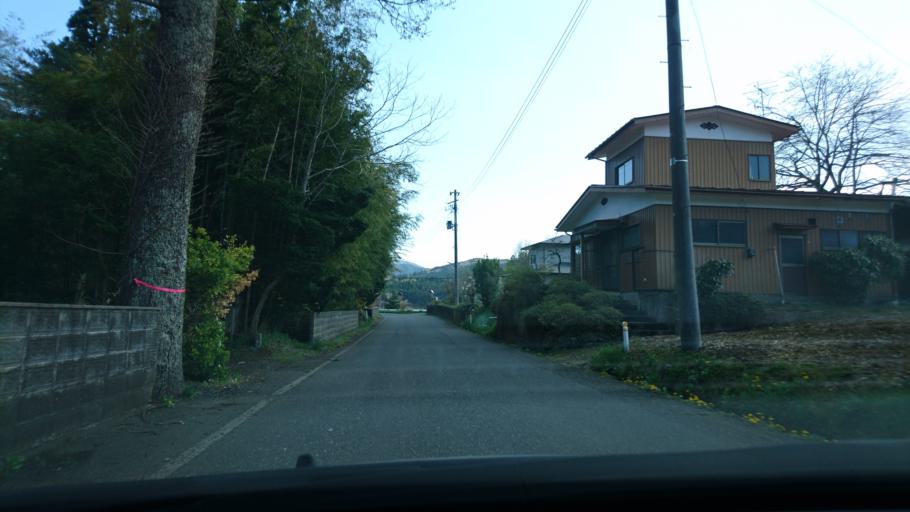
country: JP
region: Iwate
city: Ofunato
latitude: 38.9433
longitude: 141.4529
